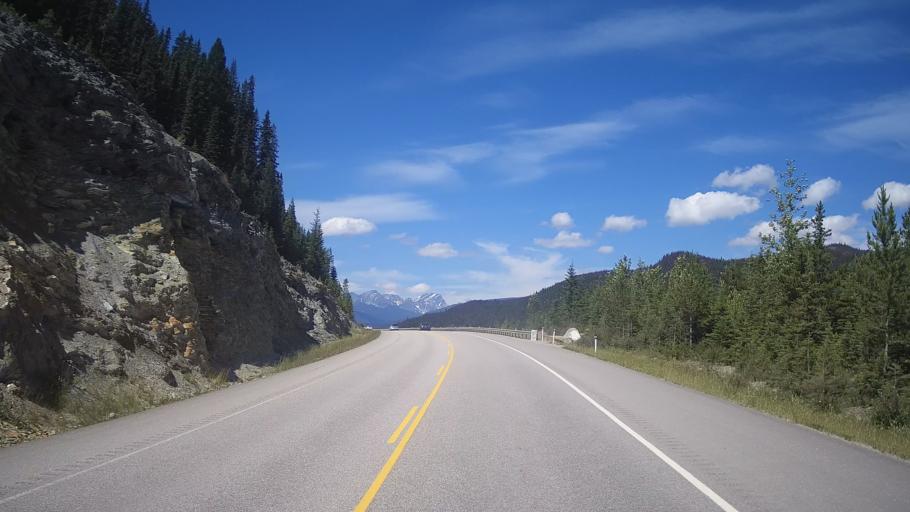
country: CA
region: Alberta
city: Jasper Park Lodge
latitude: 52.8722
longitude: -118.2803
